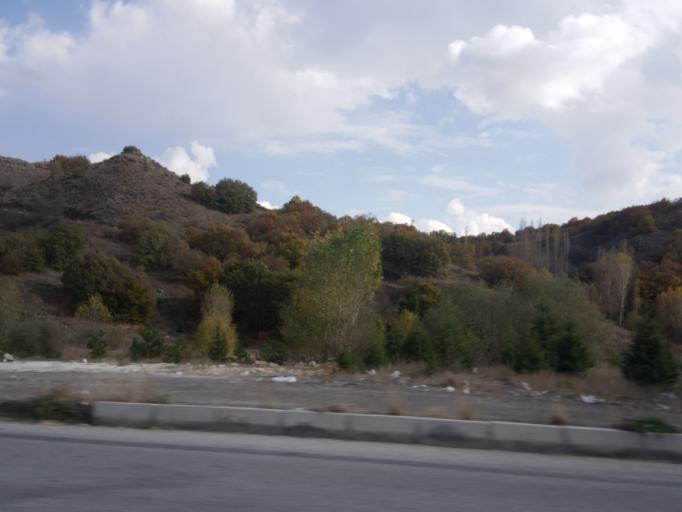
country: TR
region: Corum
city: Seydim
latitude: 40.3385
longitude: 34.7218
